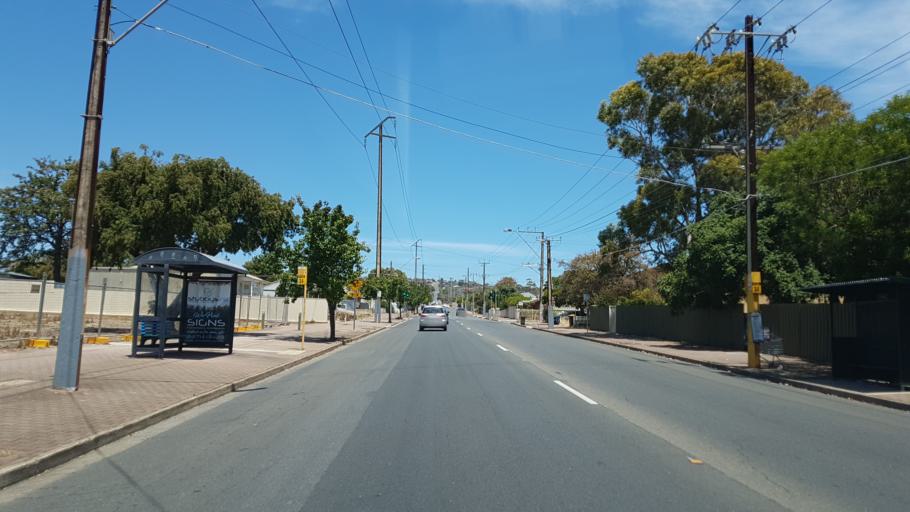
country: AU
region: South Australia
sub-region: Holdfast Bay
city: Seacliff Park
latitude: -35.0244
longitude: 138.5415
